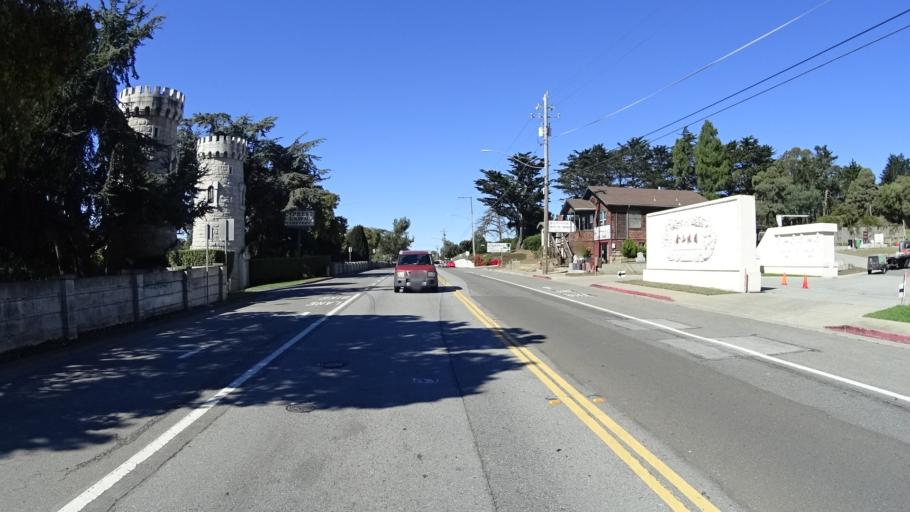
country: US
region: California
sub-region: San Mateo County
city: Colma
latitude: 37.6776
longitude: -122.4471
